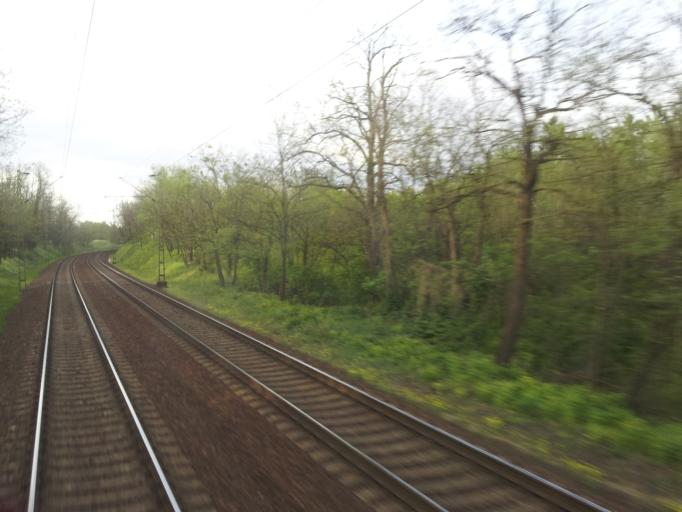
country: HU
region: Budapest
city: Budapest XV. keruelet
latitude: 47.5938
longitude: 19.1218
